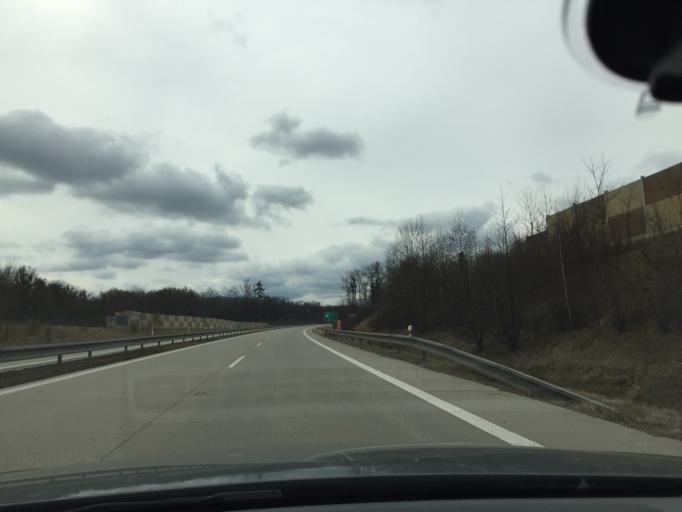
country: CZ
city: Komorni Lhotka
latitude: 49.6965
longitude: 18.5304
